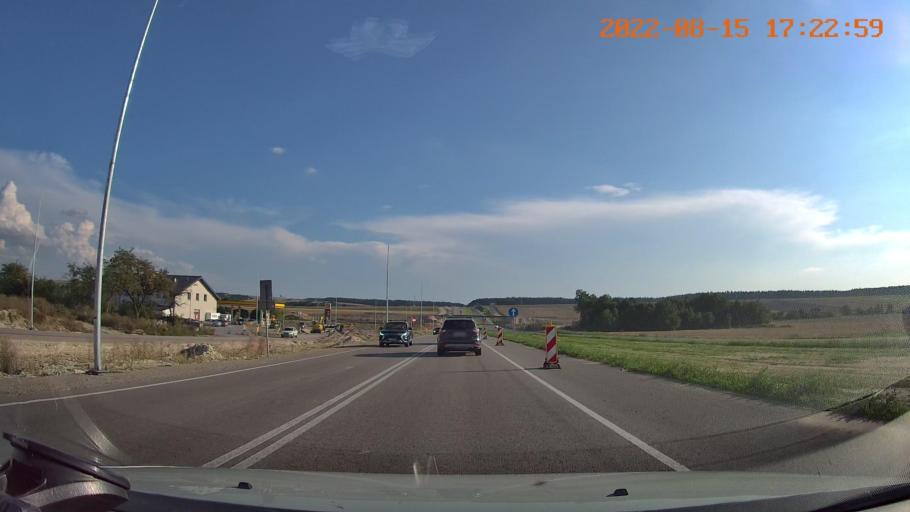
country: PL
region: Swietokrzyskie
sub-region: Powiat jedrzejowski
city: Wodzislaw
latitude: 50.4875
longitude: 20.1821
